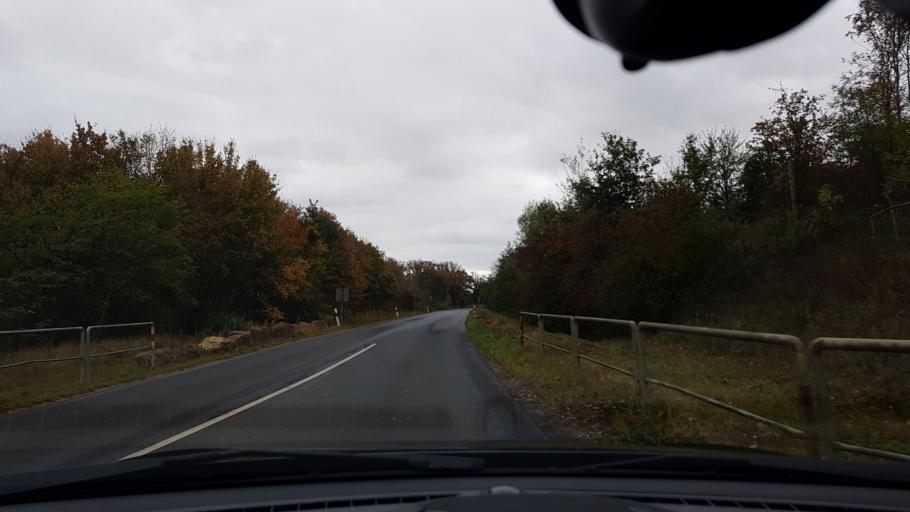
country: DE
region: North Rhine-Westphalia
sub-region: Regierungsbezirk Koln
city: Elsdorf
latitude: 50.9320
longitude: 6.5480
